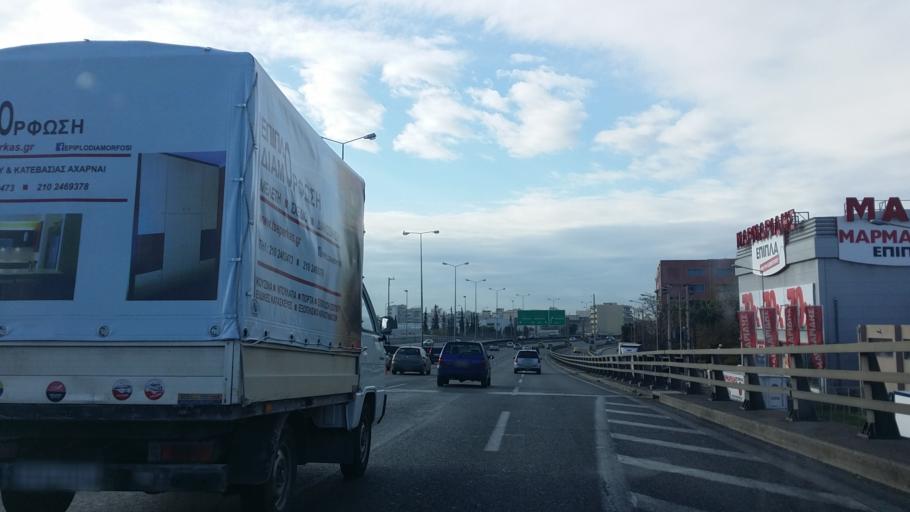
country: GR
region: Attica
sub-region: Nomarchia Athinas
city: Peristeri
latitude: 38.0063
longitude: 23.7132
